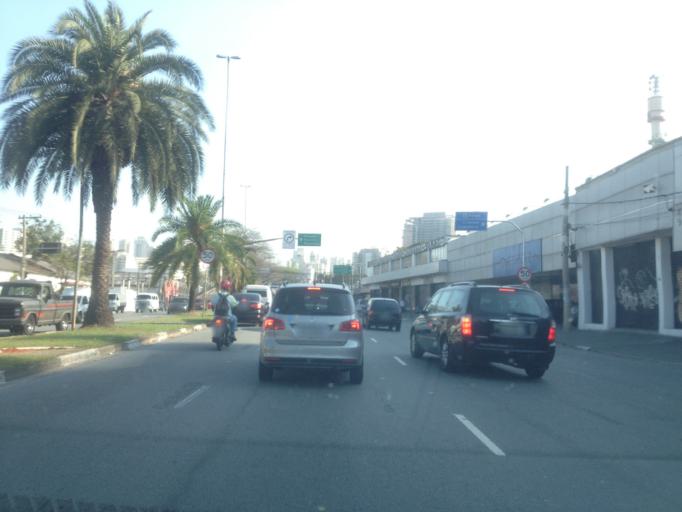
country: BR
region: Sao Paulo
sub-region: Sao Paulo
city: Sao Paulo
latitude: -23.5232
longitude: -46.6598
